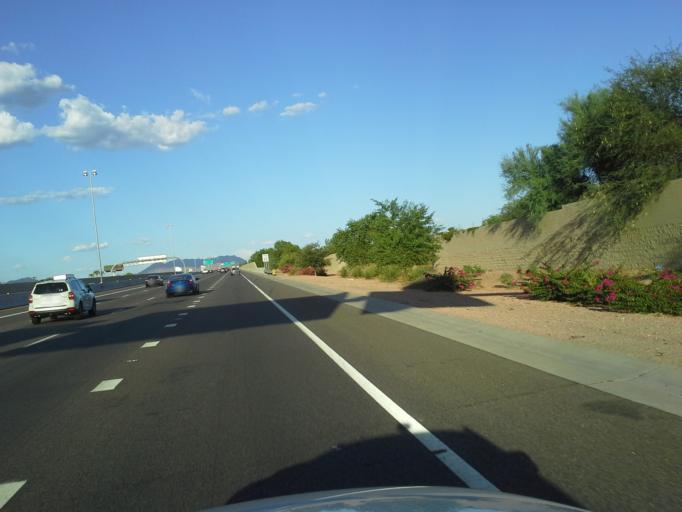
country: US
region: Arizona
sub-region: Maricopa County
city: Paradise Valley
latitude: 33.6726
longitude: -112.0202
